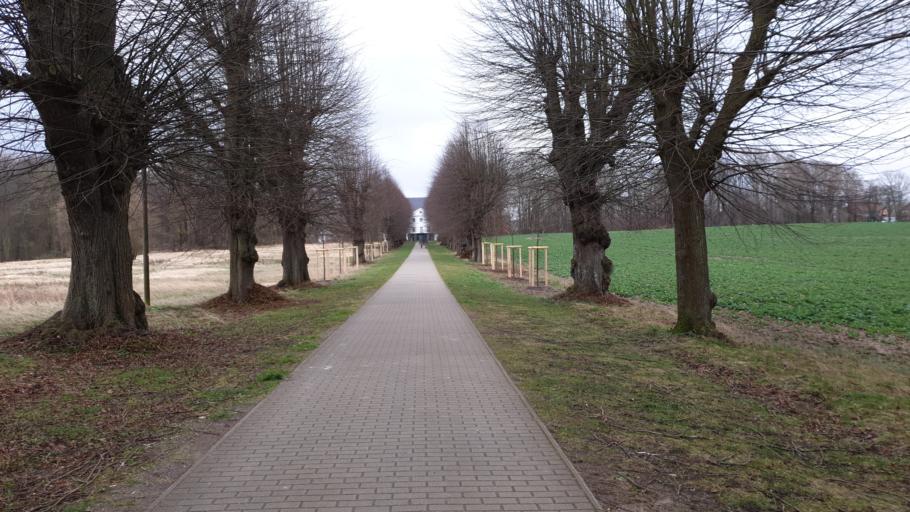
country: DE
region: Mecklenburg-Vorpommern
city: Kalkhorst
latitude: 53.9934
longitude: 11.0076
